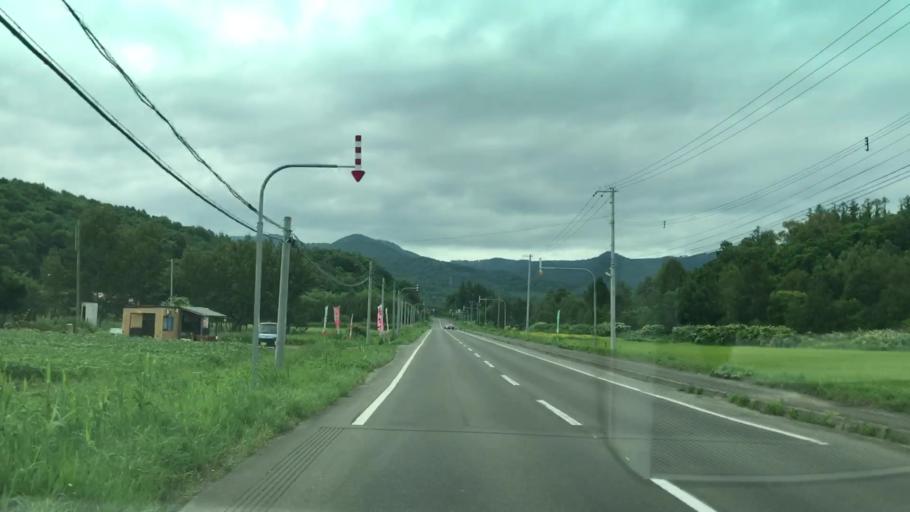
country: JP
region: Hokkaido
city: Yoichi
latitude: 43.0579
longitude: 140.8211
